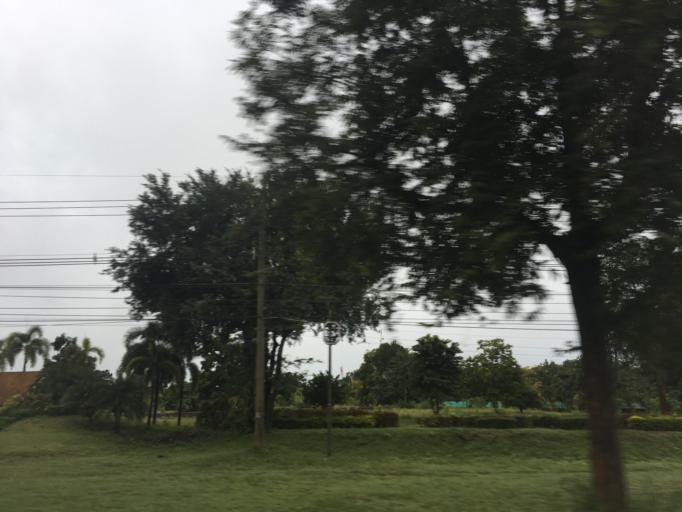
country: TH
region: Kanchanaburi
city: Sai Yok
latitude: 14.1310
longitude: 99.1619
